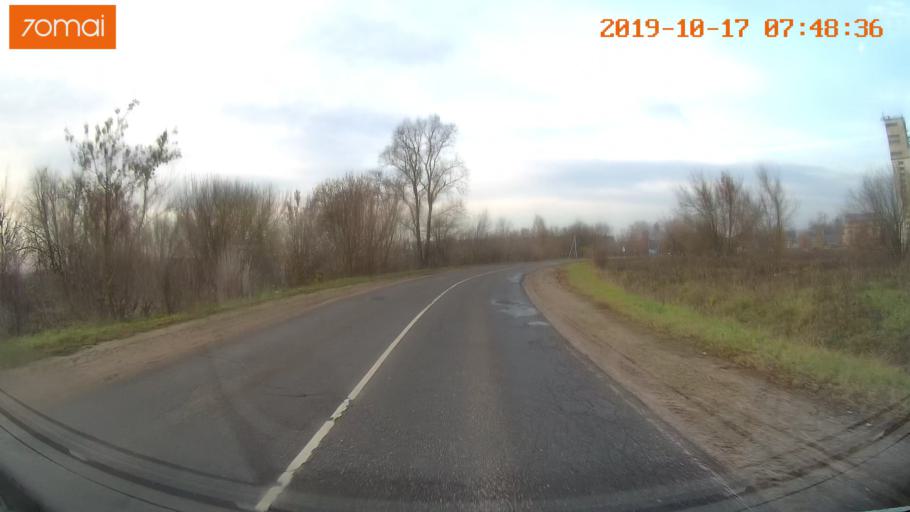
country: RU
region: Vladimir
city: Yur'yev-Pol'skiy
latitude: 56.4784
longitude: 39.6743
